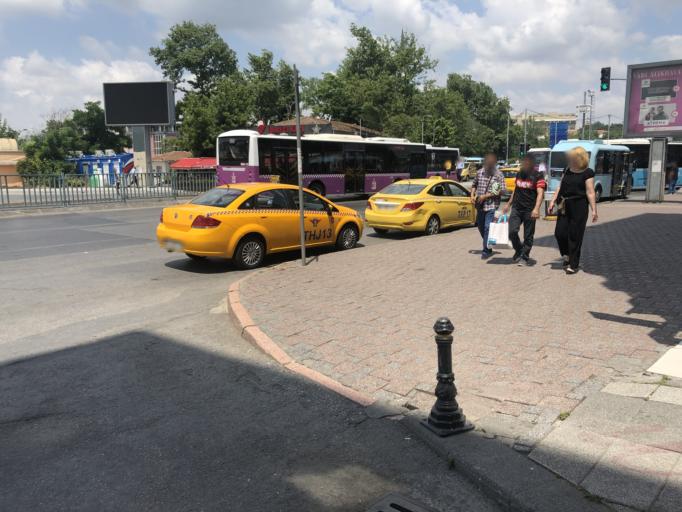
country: TR
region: Istanbul
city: UEskuedar
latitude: 40.9955
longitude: 29.0248
